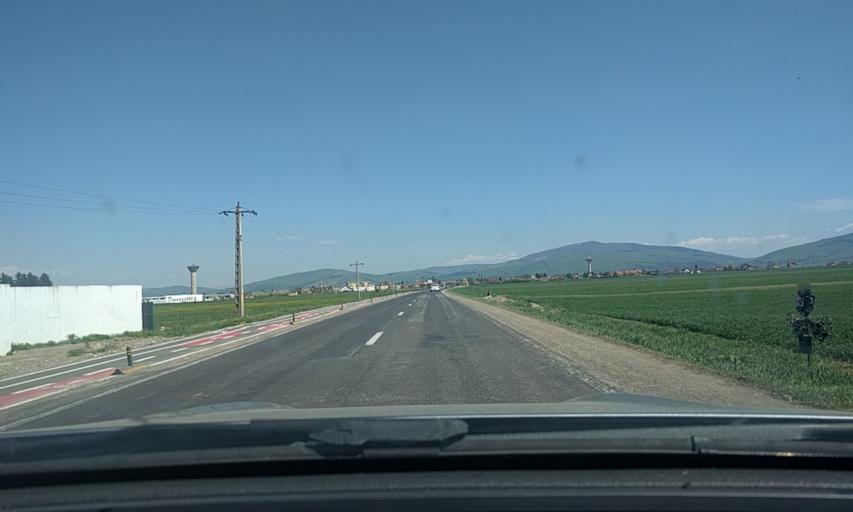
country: RO
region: Brasov
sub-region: Comuna Prejmer
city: Prejmer
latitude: 45.7165
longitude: 25.7516
